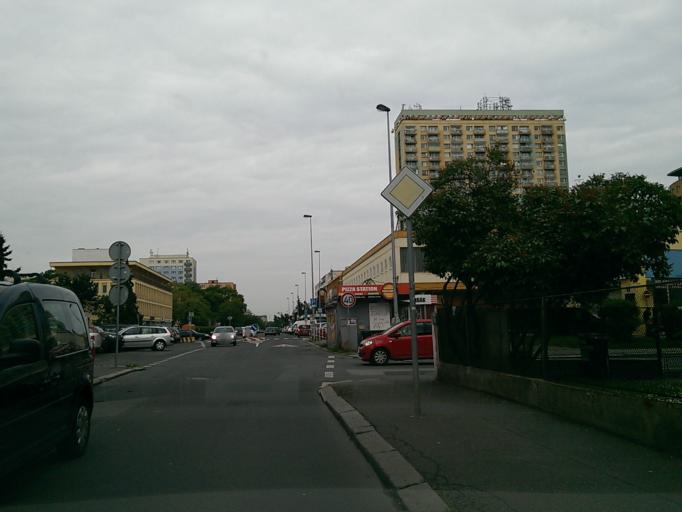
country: CZ
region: Praha
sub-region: Praha 9
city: Vysocany
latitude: 50.0565
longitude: 14.4989
